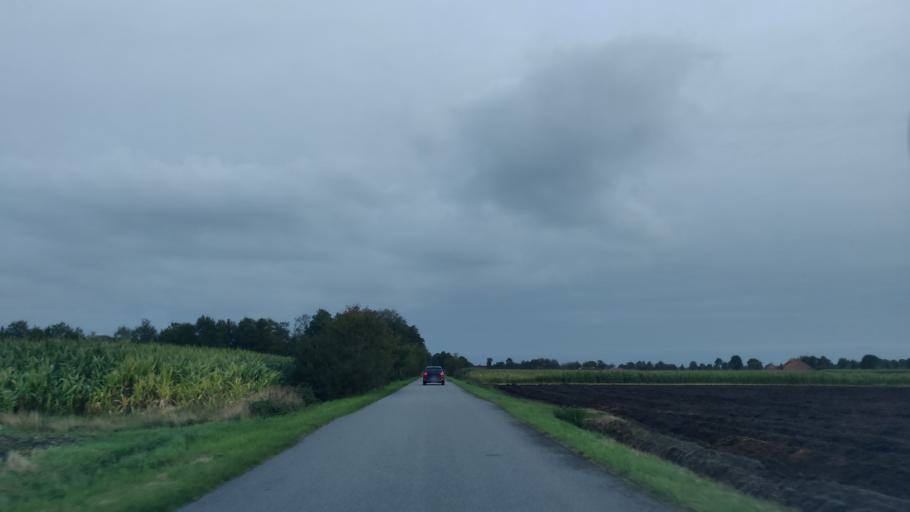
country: DE
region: Lower Saxony
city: Aurich
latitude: 53.4988
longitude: 7.4339
